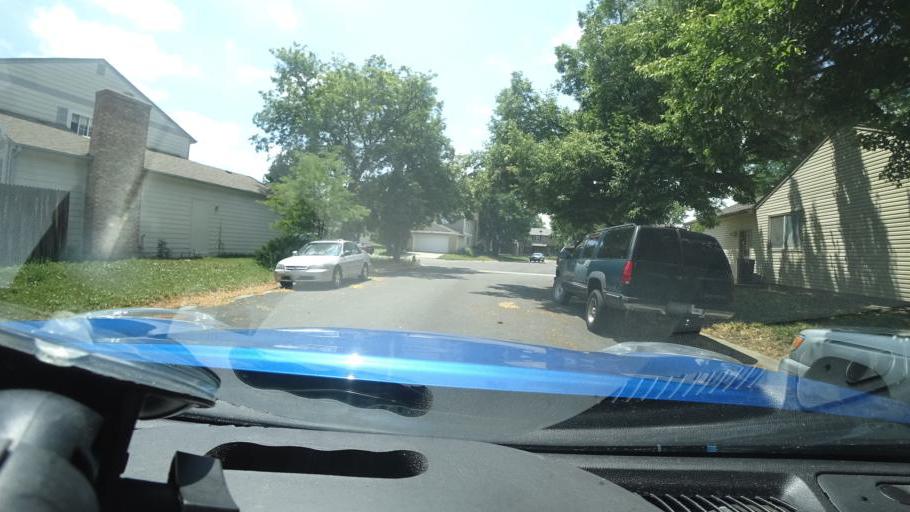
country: US
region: Colorado
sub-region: Adams County
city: Aurora
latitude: 39.7082
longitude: -104.8584
